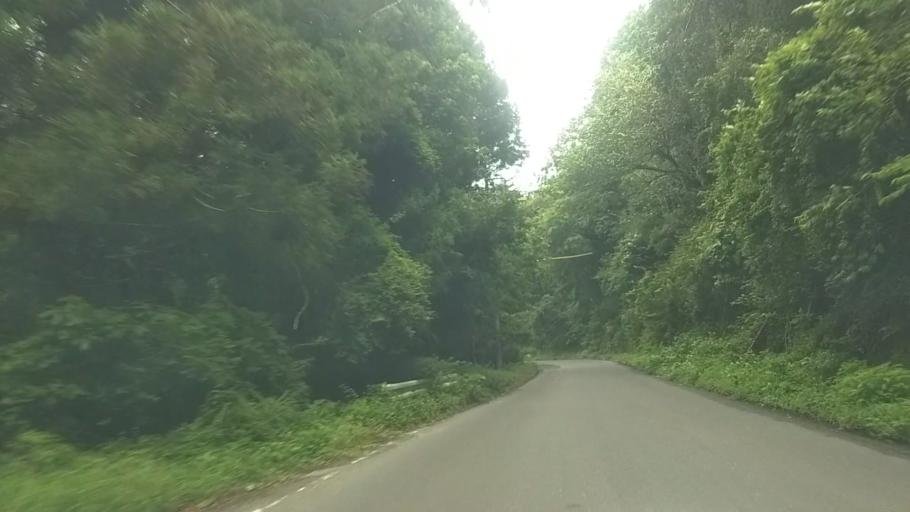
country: JP
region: Chiba
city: Kawaguchi
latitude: 35.2260
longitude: 140.0262
